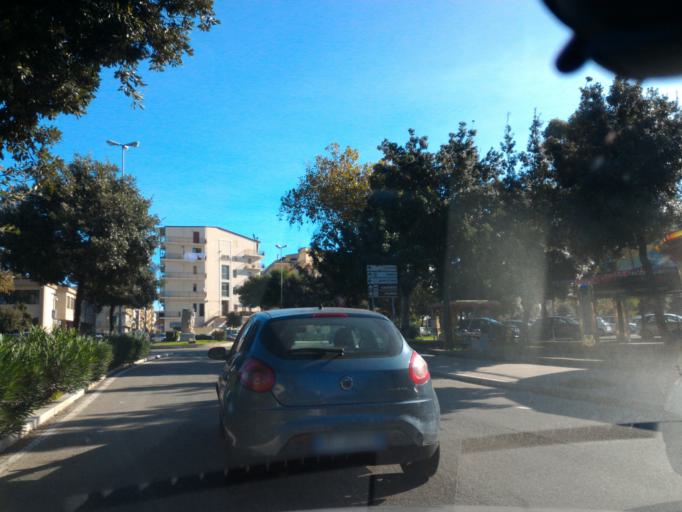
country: IT
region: Calabria
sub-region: Provincia di Crotone
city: Crotone
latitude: 39.0805
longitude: 17.1218
